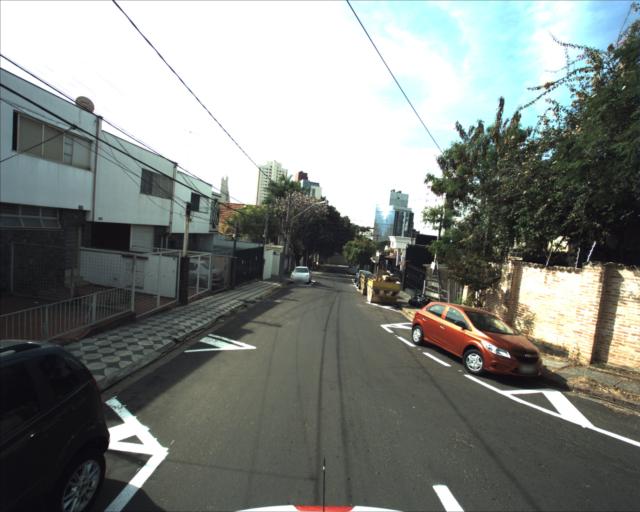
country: BR
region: Sao Paulo
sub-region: Sorocaba
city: Sorocaba
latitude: -23.5072
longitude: -47.4610
